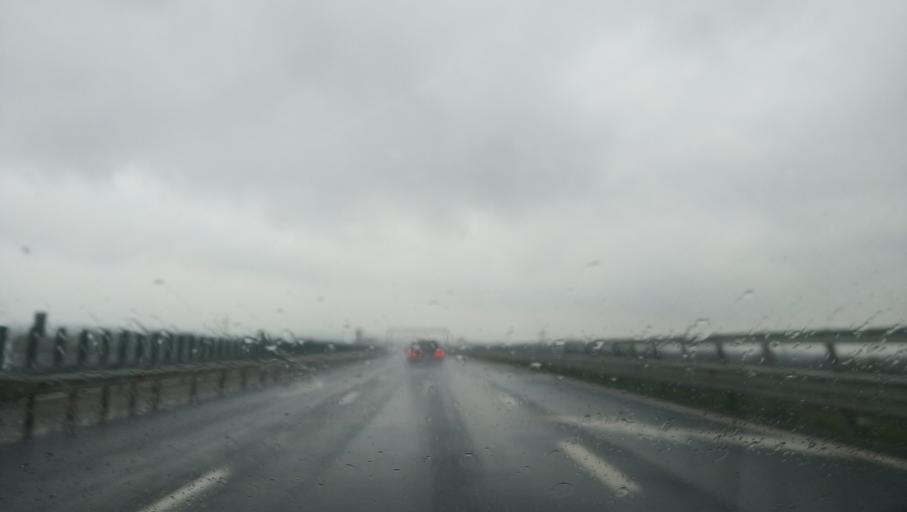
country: RO
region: Timis
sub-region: Comuna Margina
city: Margina
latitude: 45.8558
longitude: 22.2415
